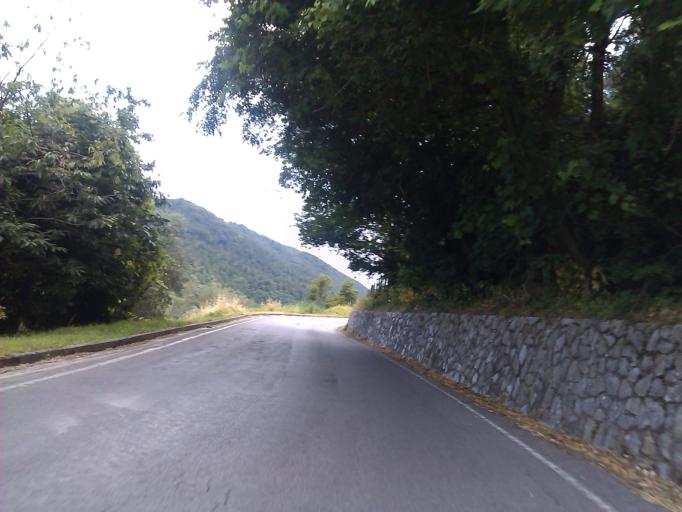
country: IT
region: Tuscany
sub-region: Provincia di Prato
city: Montemurlo
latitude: 43.9600
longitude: 11.0446
